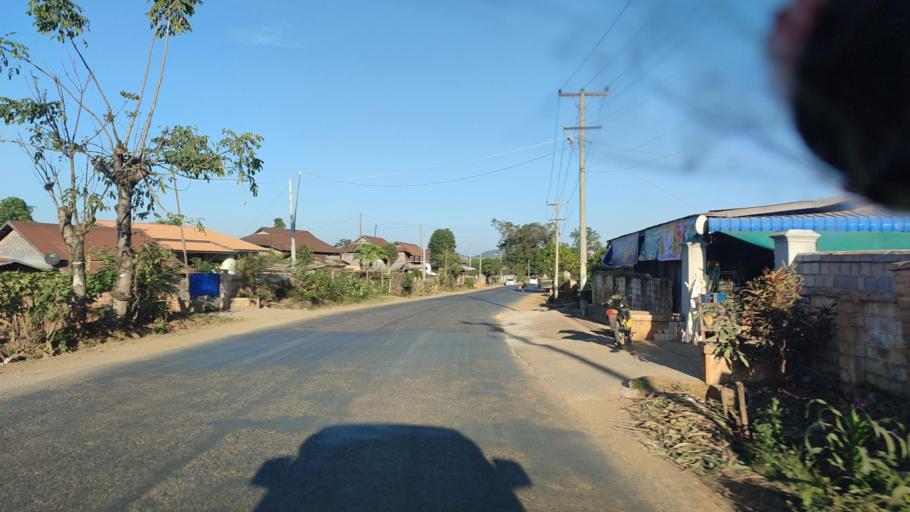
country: MM
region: Mandalay
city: Mogok
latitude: 22.5055
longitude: 97.0148
